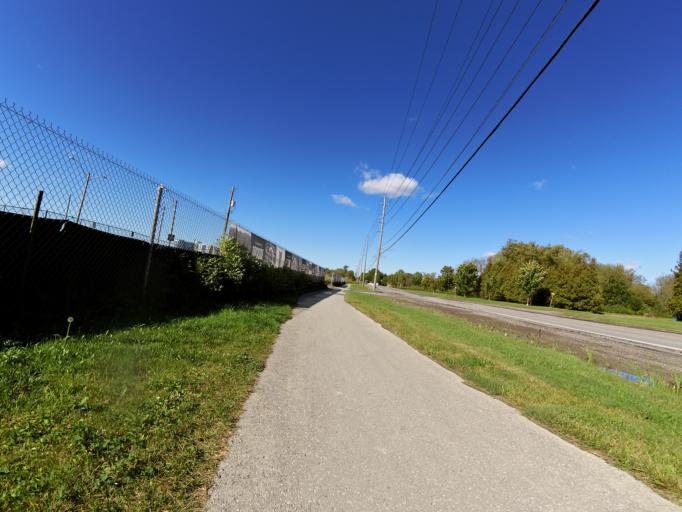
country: CA
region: Ontario
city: Oshawa
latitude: 43.8548
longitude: -78.9316
